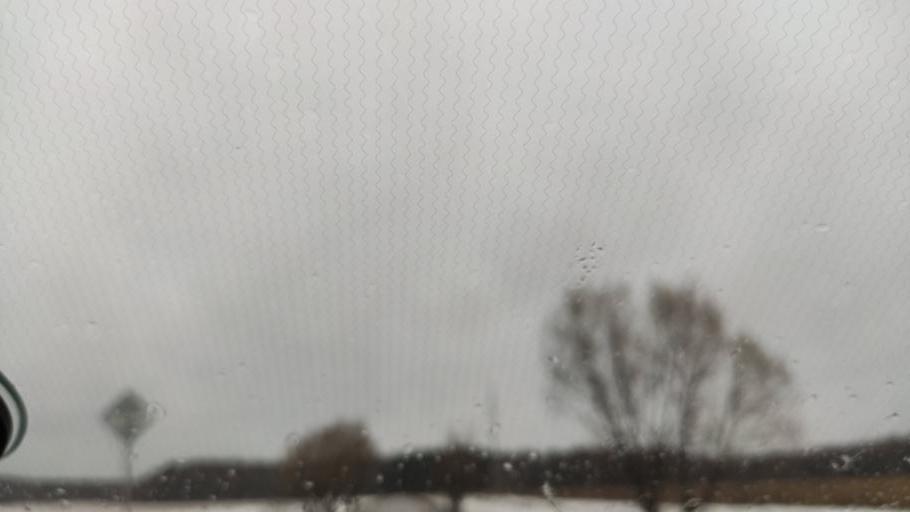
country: RU
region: Moskovskaya
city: Vatutinki
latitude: 55.4662
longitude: 37.3544
